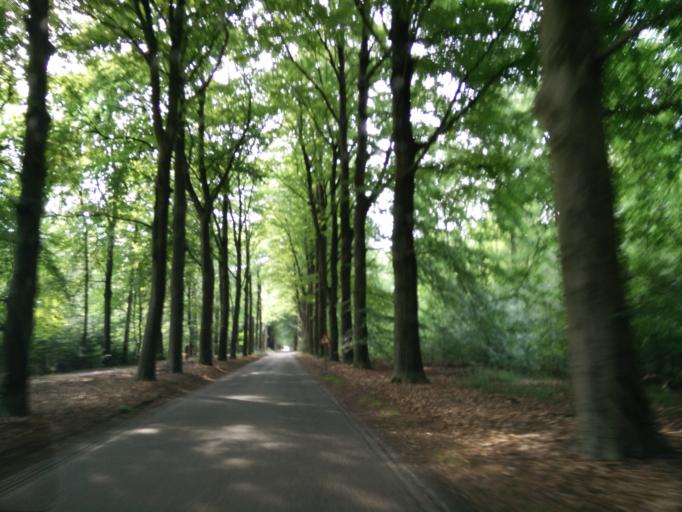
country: NL
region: Drenthe
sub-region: Gemeente Aa en Hunze
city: Anloo
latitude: 52.9830
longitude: 6.7317
